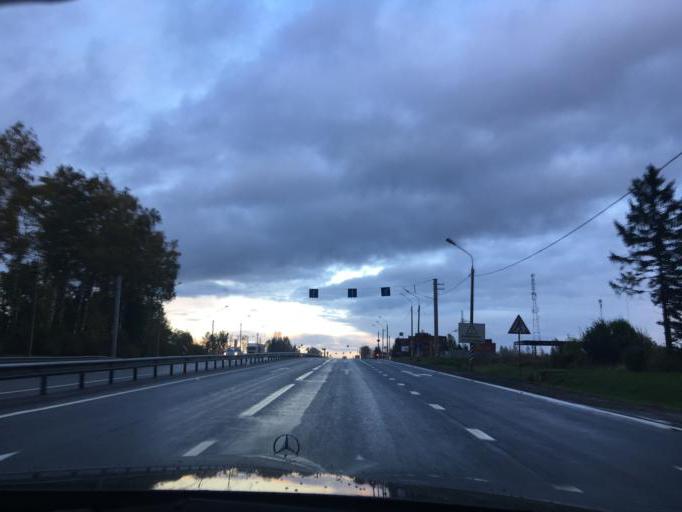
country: RU
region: Smolensk
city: Yartsevo
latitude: 55.0648
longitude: 32.6167
